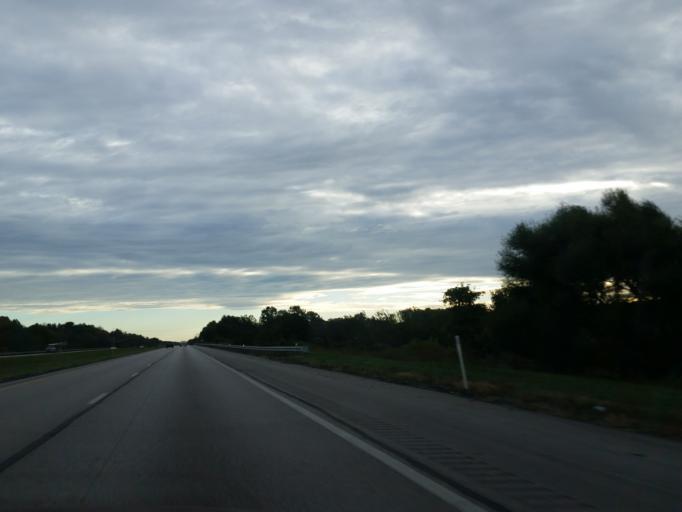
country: US
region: Ohio
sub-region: Ashtabula County
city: Conneaut
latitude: 41.9269
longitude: -80.5399
